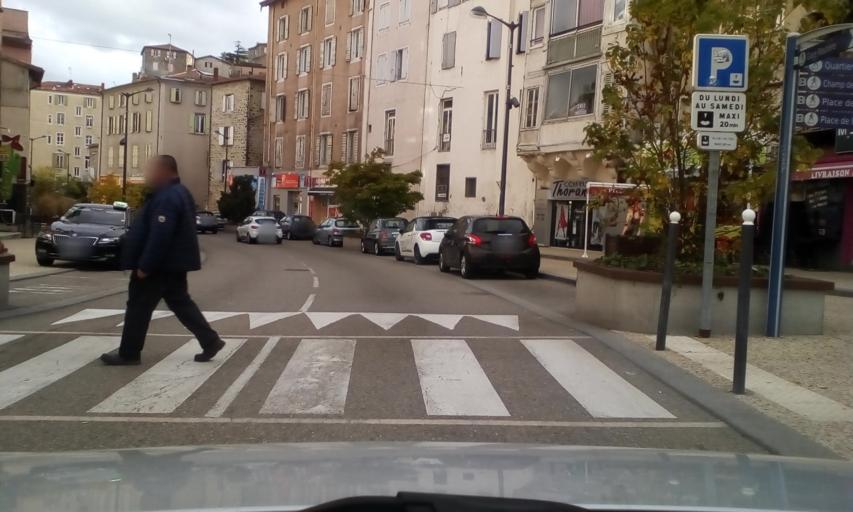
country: FR
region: Rhone-Alpes
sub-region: Departement de l'Ardeche
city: Annonay
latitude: 45.2409
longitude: 4.6716
